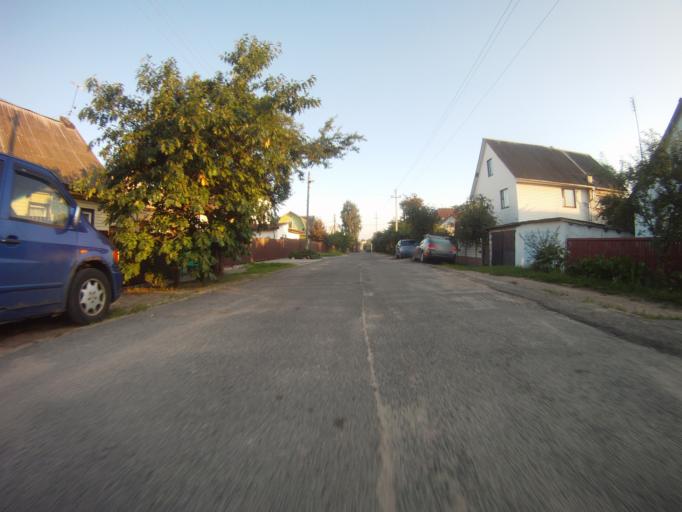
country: BY
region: Minsk
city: Minsk
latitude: 53.9368
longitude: 27.5591
